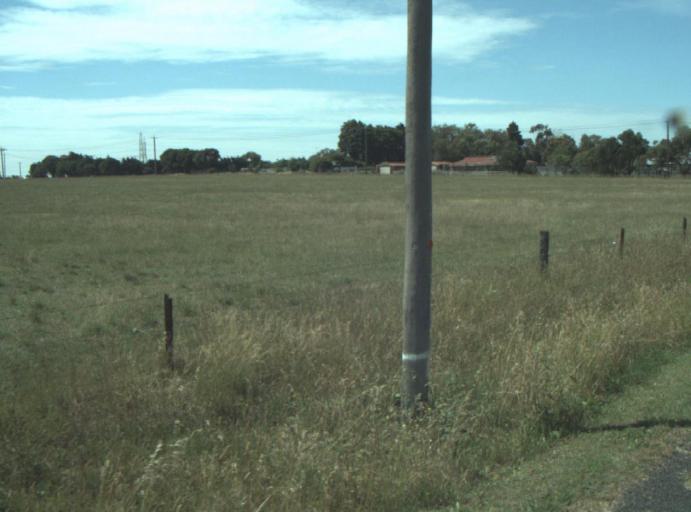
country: AU
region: Victoria
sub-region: Greater Geelong
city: East Geelong
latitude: -38.1710
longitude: 144.4181
